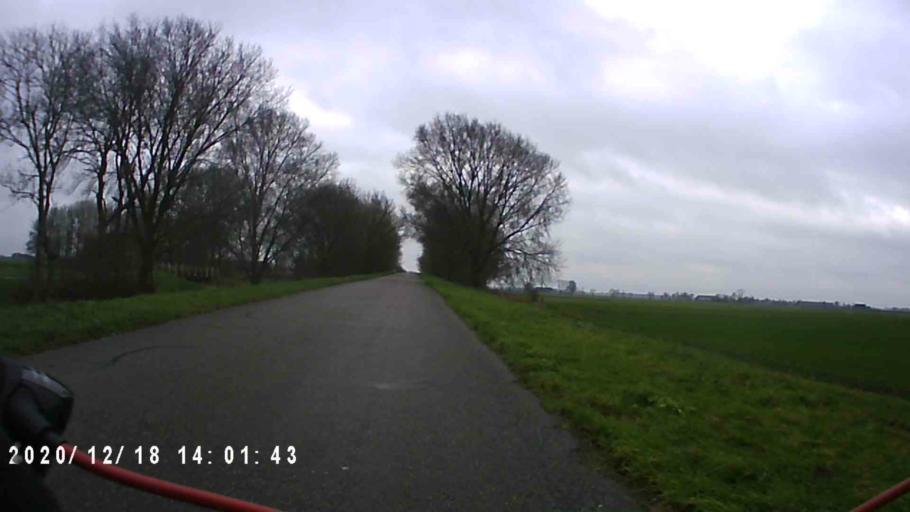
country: NL
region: Groningen
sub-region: Gemeente Bedum
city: Bedum
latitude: 53.2952
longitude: 6.6425
